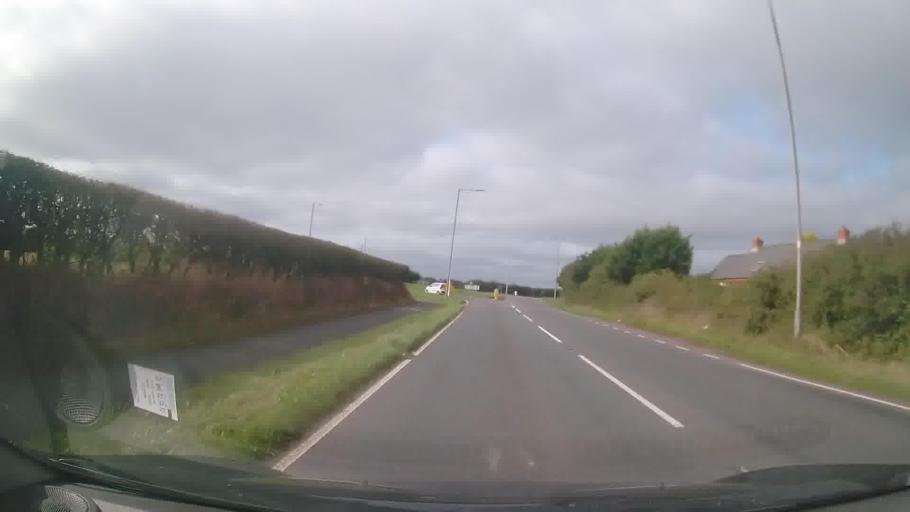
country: GB
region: Wales
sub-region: Pembrokeshire
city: Johnston
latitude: 51.7312
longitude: -4.9902
